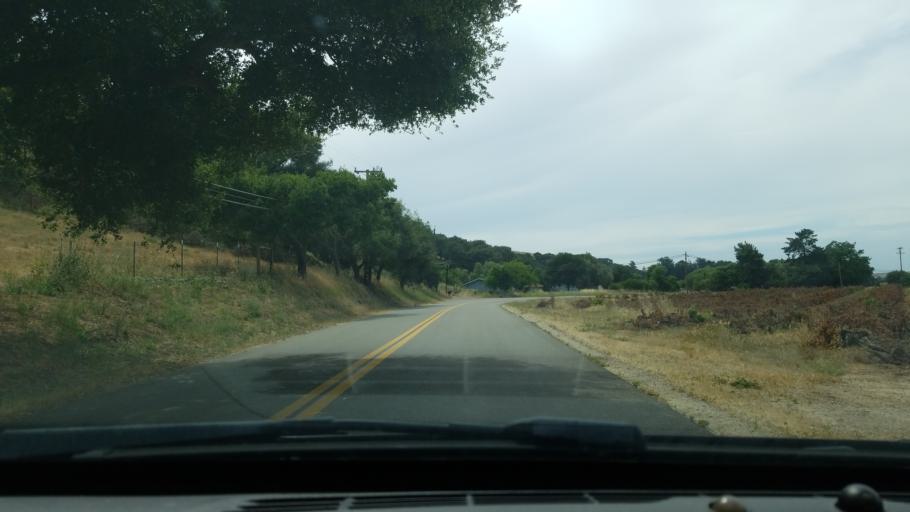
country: US
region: California
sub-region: Santa Barbara County
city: Los Alamos
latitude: 34.8536
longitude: -120.2627
